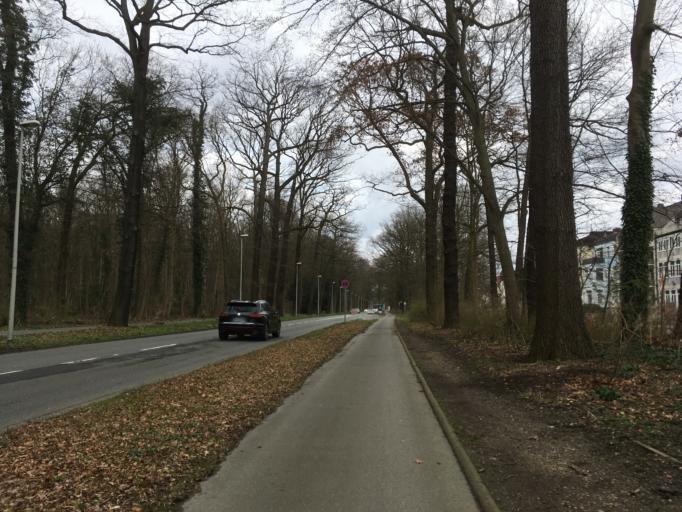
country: DE
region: Lower Saxony
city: Hannover
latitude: 52.3793
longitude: 9.7597
